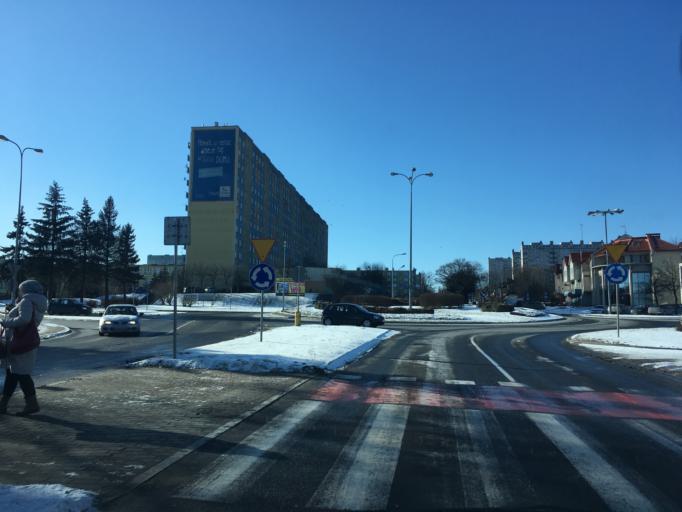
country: PL
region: Pomeranian Voivodeship
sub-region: Slupsk
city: Slupsk
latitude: 54.4731
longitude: 17.0141
